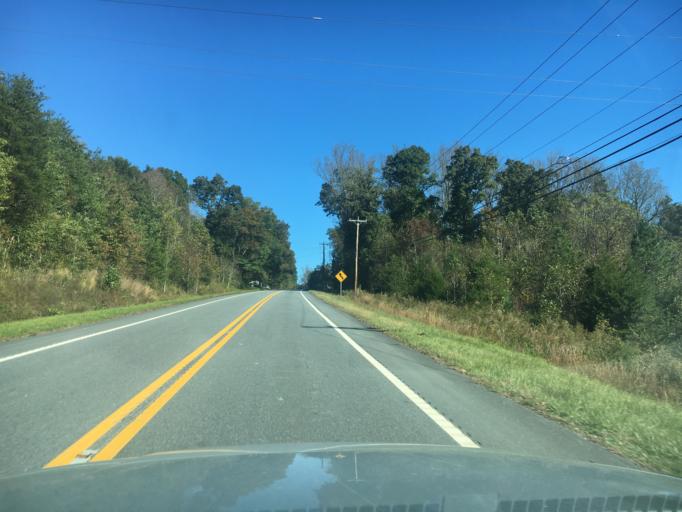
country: US
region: North Carolina
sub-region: Rutherford County
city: Spindale
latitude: 35.3979
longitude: -81.9260
